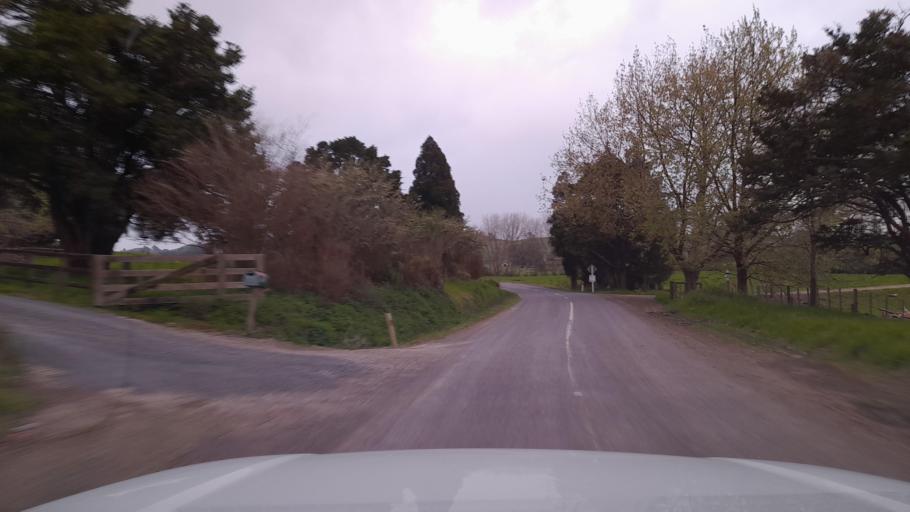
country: NZ
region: Northland
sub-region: Whangarei
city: Maungatapere
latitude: -35.6320
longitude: 174.1991
